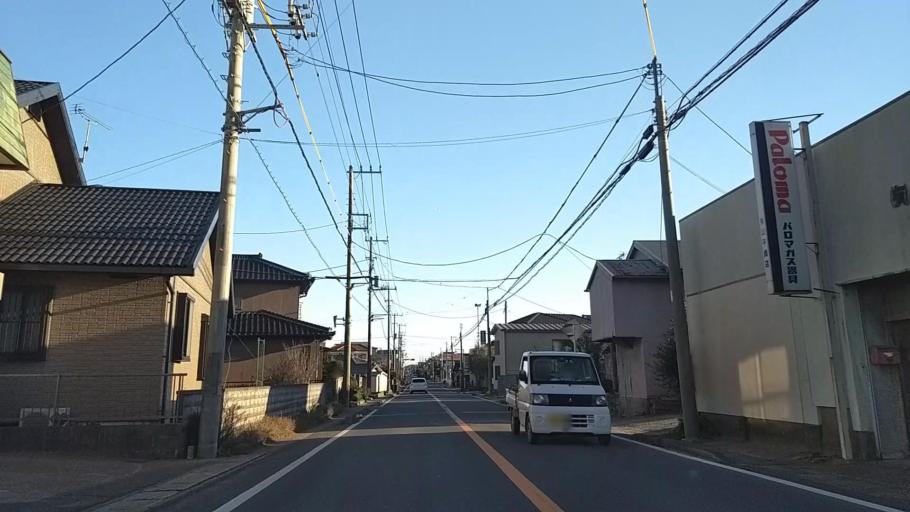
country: JP
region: Chiba
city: Hasaki
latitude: 35.7626
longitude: 140.7662
